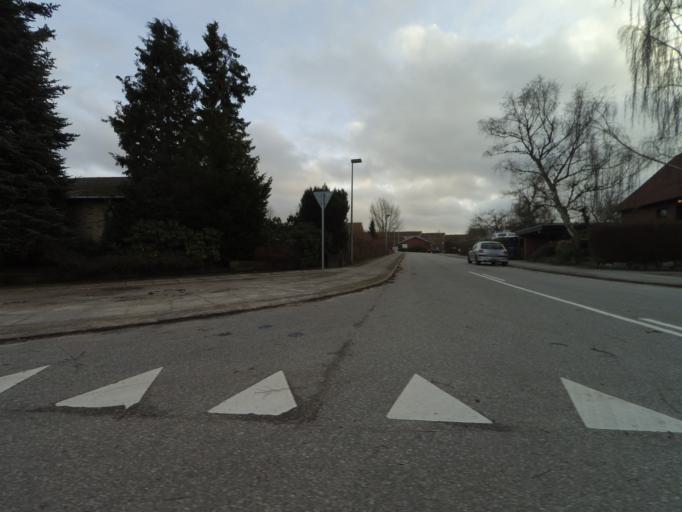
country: DK
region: Central Jutland
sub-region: Arhus Kommune
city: Arhus
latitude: 56.1228
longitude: 10.1766
